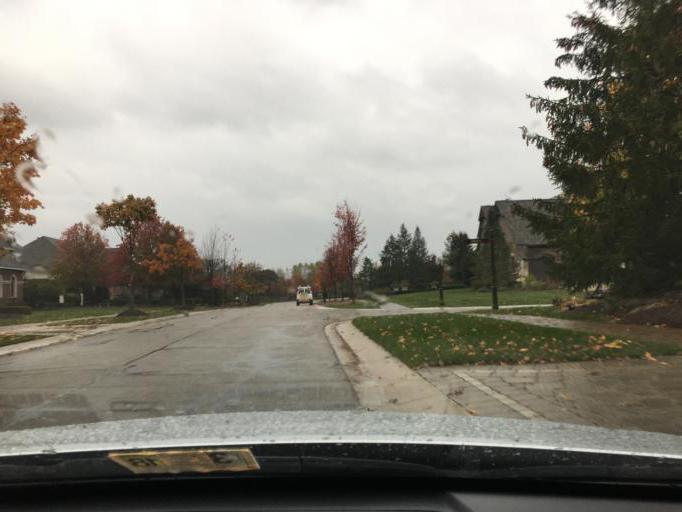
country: US
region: Michigan
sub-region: Oakland County
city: Auburn Hills
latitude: 42.7185
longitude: -83.1981
